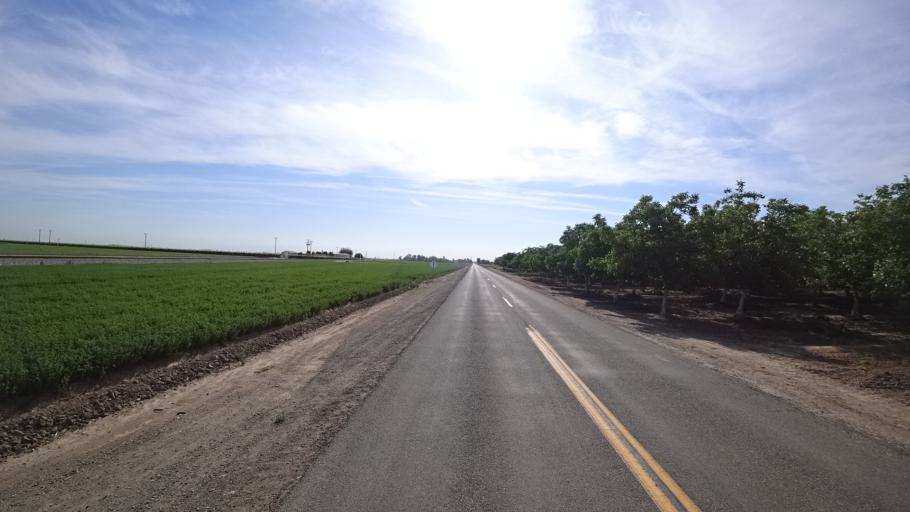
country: US
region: California
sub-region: Tulare County
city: Goshen
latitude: 36.3492
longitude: -119.4865
